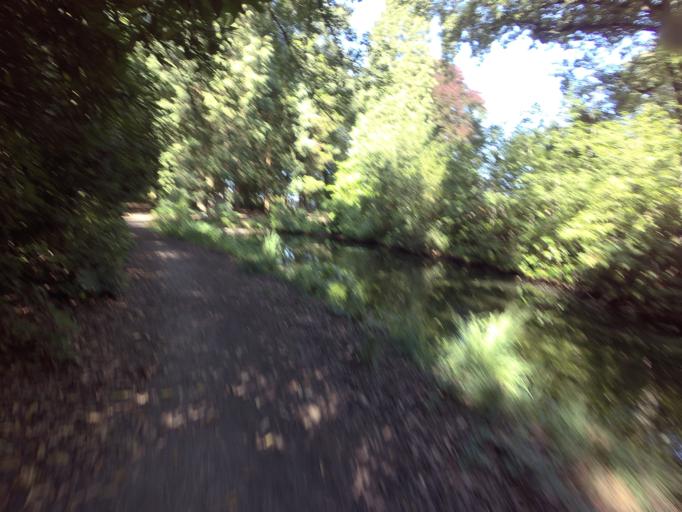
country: DE
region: North Rhine-Westphalia
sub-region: Regierungsbezirk Koln
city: Wassenberg
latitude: 51.1567
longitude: 6.1584
